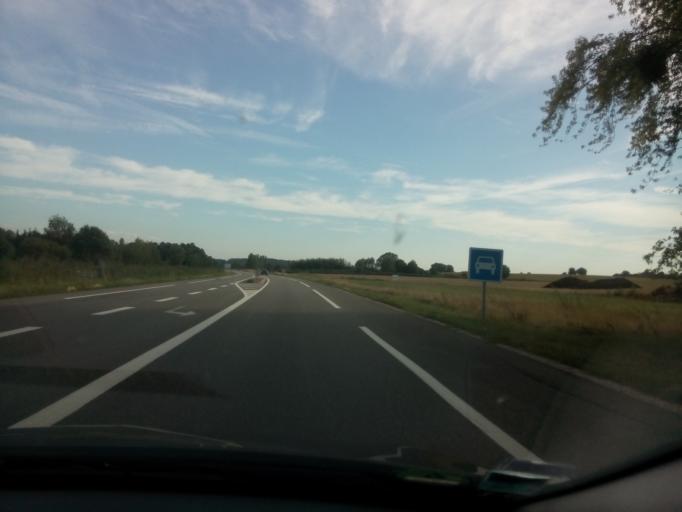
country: FR
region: Alsace
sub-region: Departement du Bas-Rhin
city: Soultz-sous-Forets
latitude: 48.9615
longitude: 7.9532
